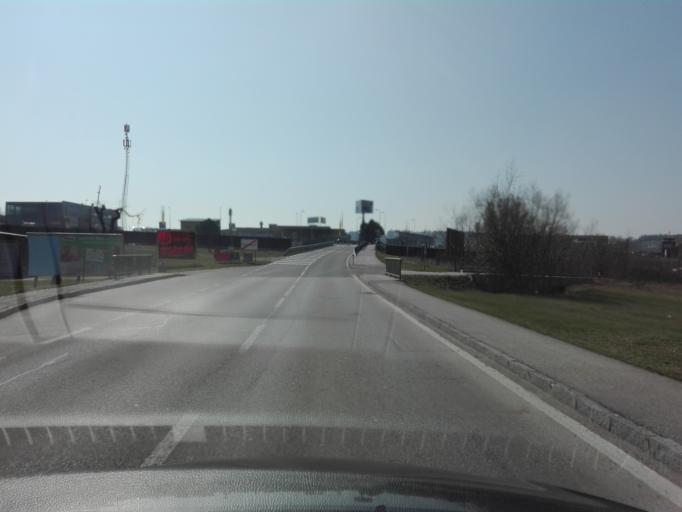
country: AT
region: Upper Austria
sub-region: Politischer Bezirk Urfahr-Umgebung
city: Engerwitzdorf
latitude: 48.3600
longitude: 14.4747
